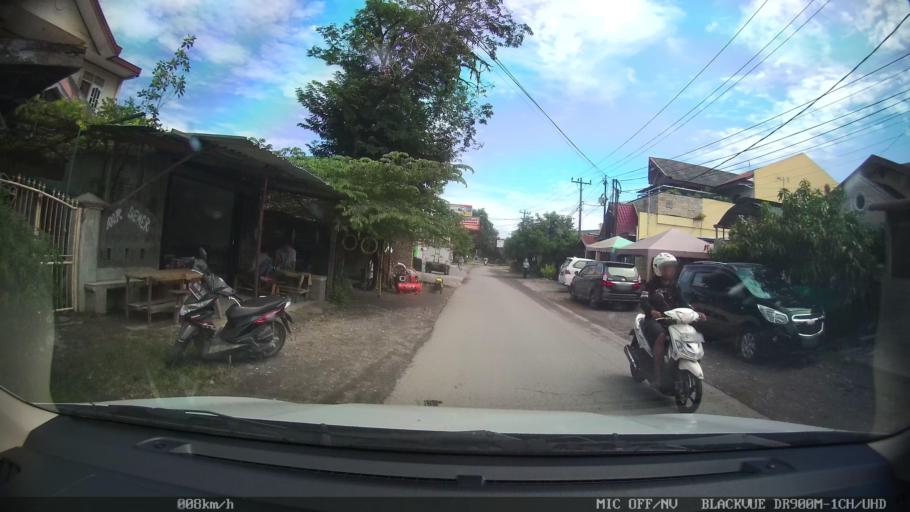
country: ID
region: North Sumatra
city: Medan
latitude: 3.5867
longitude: 98.7344
